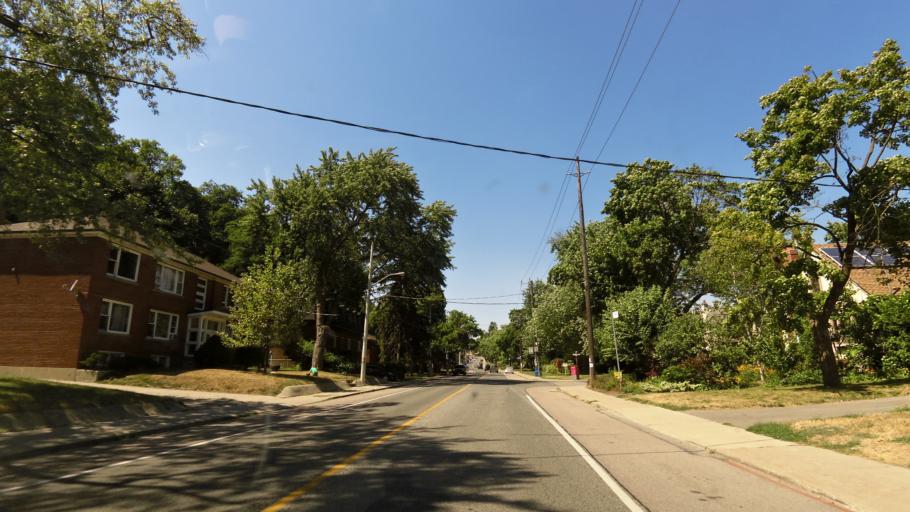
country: CA
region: Ontario
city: Etobicoke
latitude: 43.6444
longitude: -79.4821
